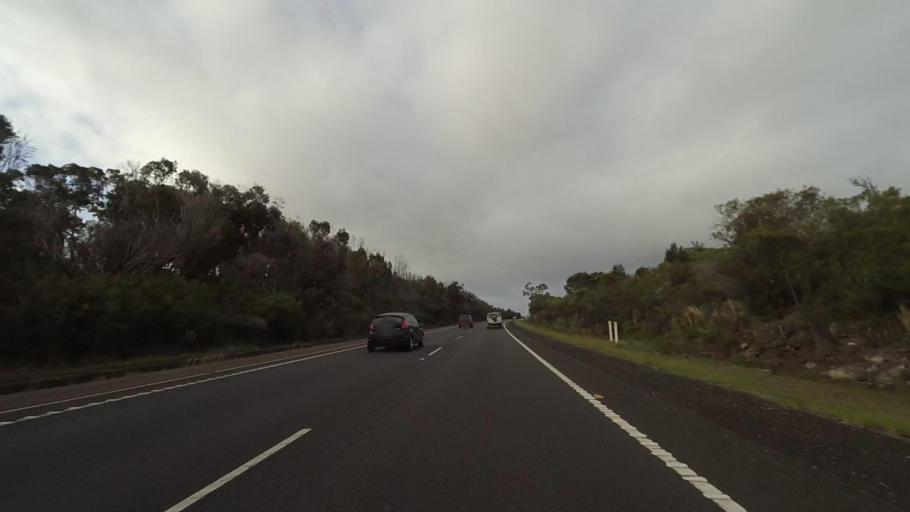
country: AU
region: New South Wales
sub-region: Wollongong
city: Bulli
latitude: -34.2667
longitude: 150.9268
